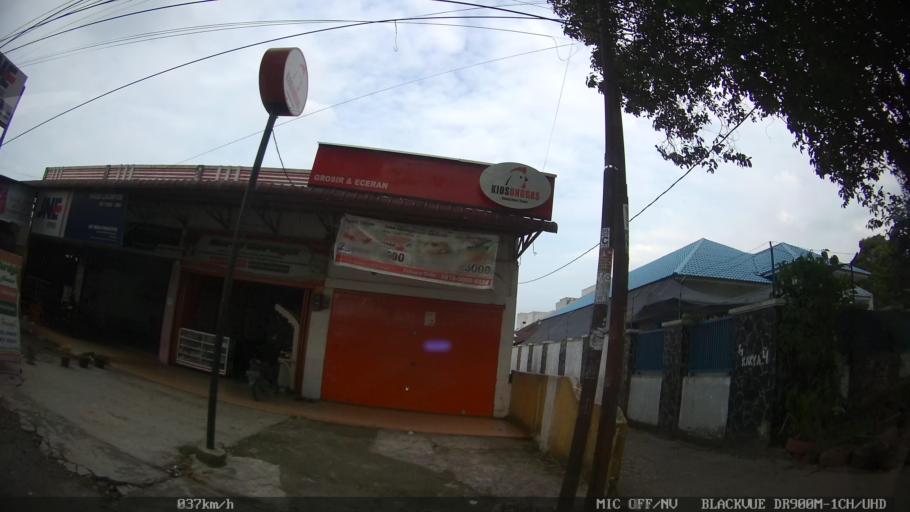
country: ID
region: North Sumatra
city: Deli Tua
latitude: 3.5434
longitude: 98.6796
